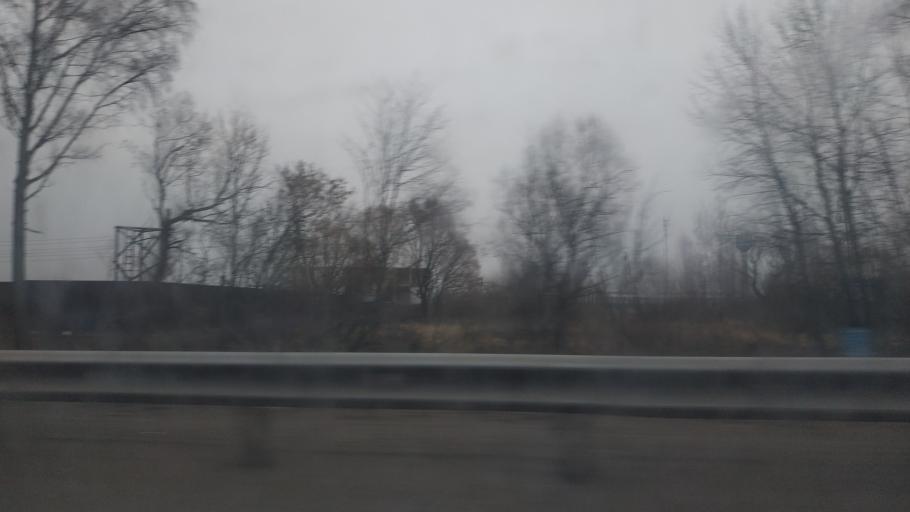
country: RU
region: Moskovskaya
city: Marfino
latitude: 56.0142
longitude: 37.5466
